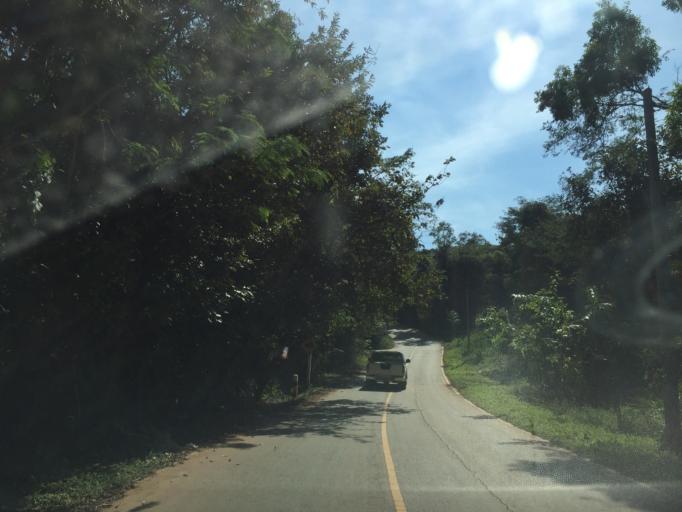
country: TH
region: Chiang Mai
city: Samoeng
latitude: 18.9452
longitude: 98.7958
